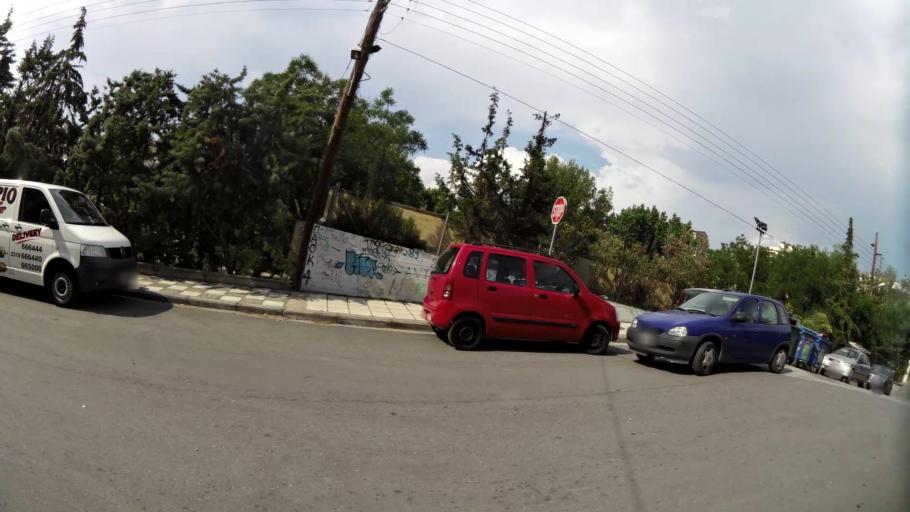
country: GR
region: Central Macedonia
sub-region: Nomos Thessalonikis
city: Polichni
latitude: 40.6596
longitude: 22.9465
